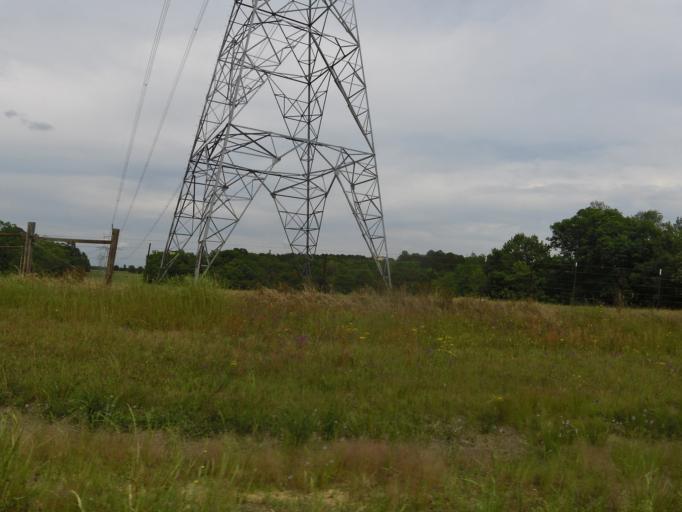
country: US
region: Georgia
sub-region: McDuffie County
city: Thomson
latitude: 33.3712
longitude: -82.4680
